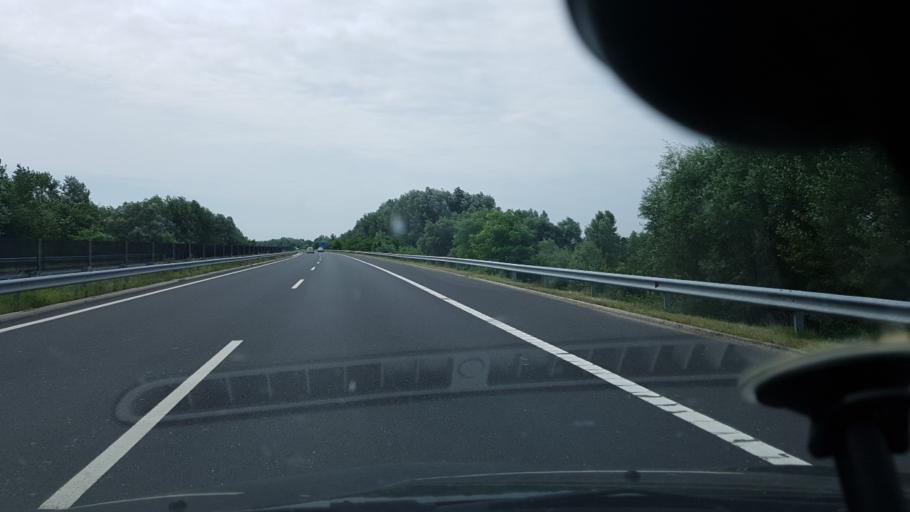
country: HU
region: Zala
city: Zalakomar
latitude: 46.5499
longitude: 17.2156
